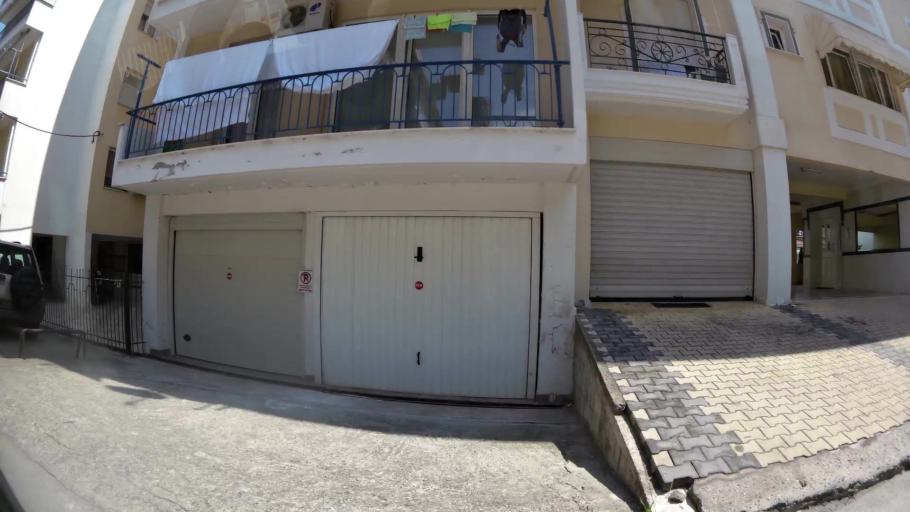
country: GR
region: Central Macedonia
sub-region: Nomos Imathias
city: Veroia
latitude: 40.5146
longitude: 22.2061
